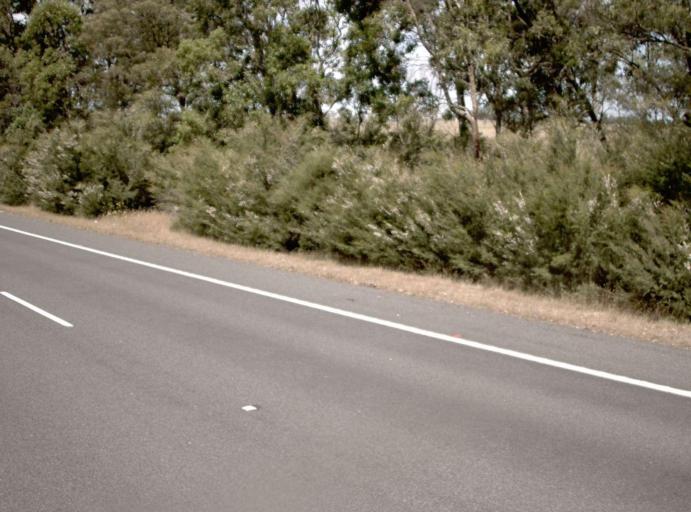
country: AU
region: Victoria
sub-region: Wellington
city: Sale
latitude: -37.9388
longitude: 147.1511
